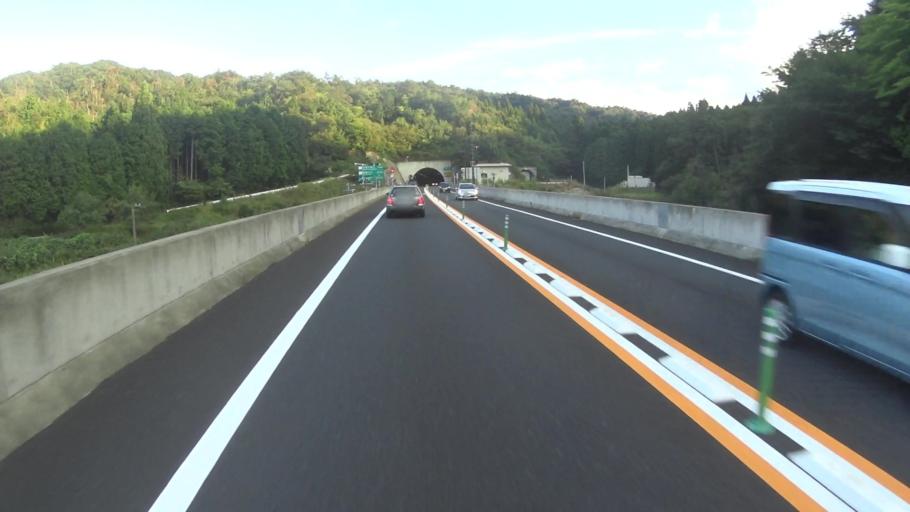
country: JP
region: Kyoto
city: Miyazu
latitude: 35.5429
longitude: 135.1552
